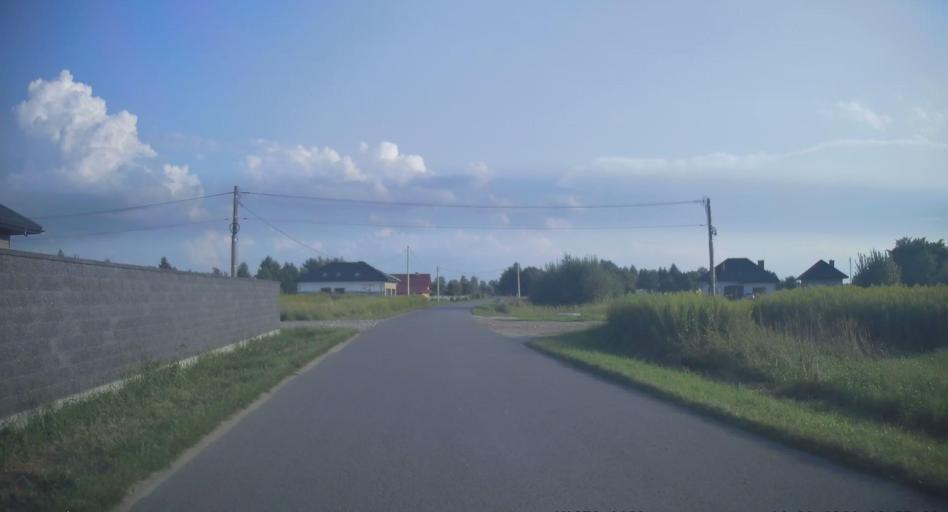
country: PL
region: Subcarpathian Voivodeship
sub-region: Powiat debicki
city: Zyrakow
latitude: 50.0849
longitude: 21.3827
